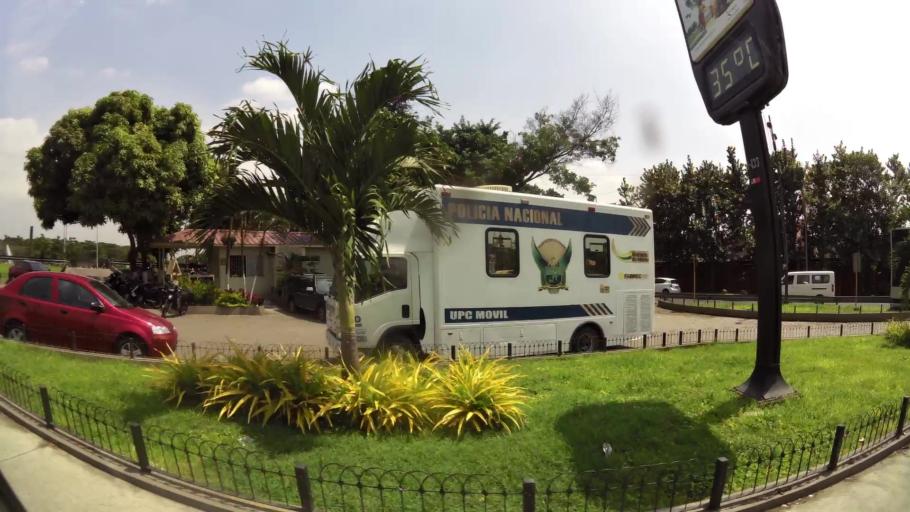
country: EC
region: Guayas
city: Eloy Alfaro
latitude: -2.1512
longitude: -79.8652
